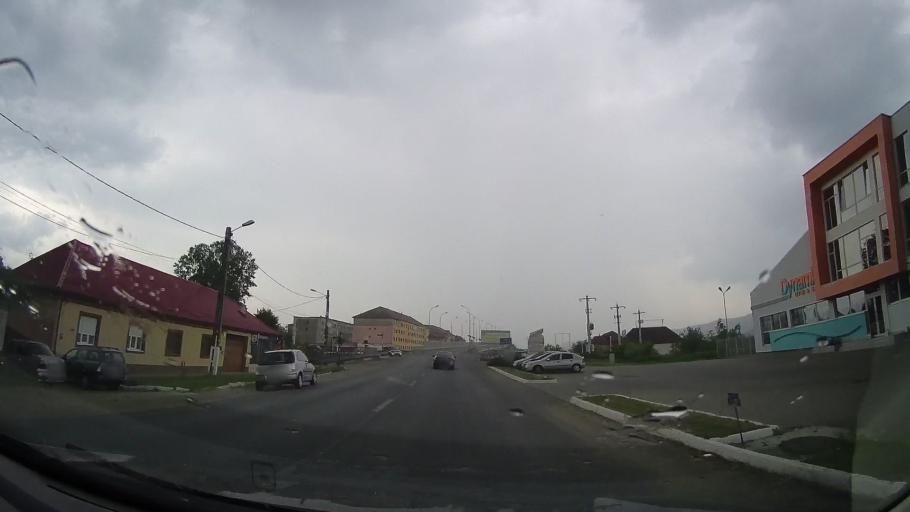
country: RO
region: Caras-Severin
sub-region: Comuna Buchin
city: Buchin
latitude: 45.3880
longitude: 22.2290
